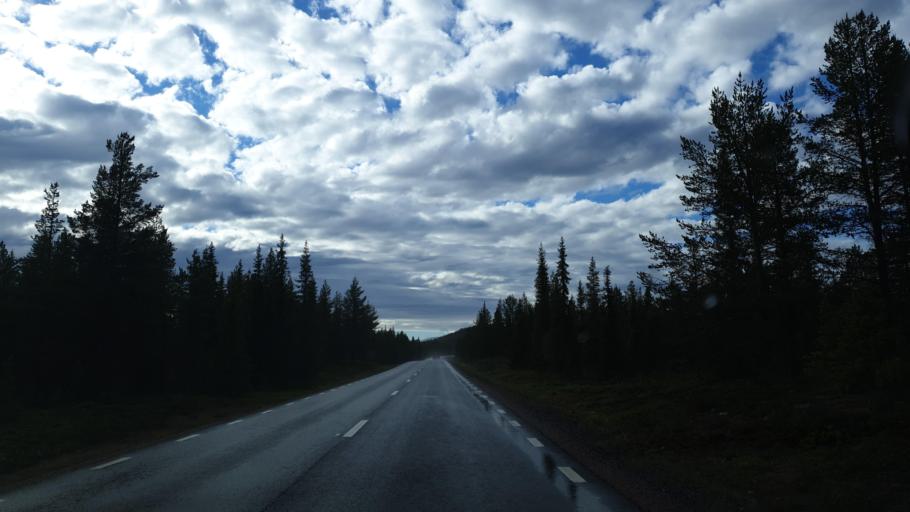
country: SE
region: Norrbotten
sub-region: Arjeplogs Kommun
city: Arjeplog
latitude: 65.8885
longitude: 18.3803
